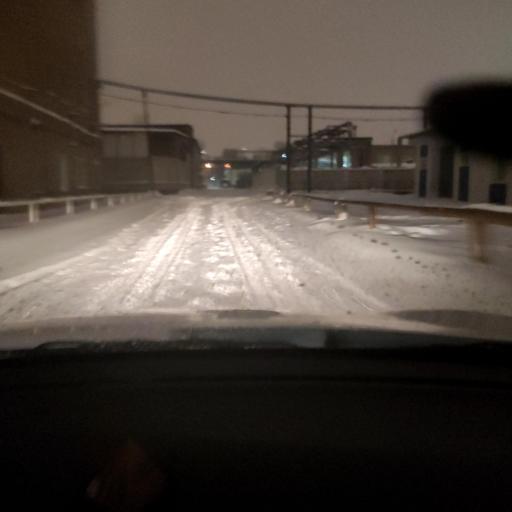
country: RU
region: Tatarstan
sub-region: Gorod Kazan'
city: Kazan
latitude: 55.8359
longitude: 49.0528
